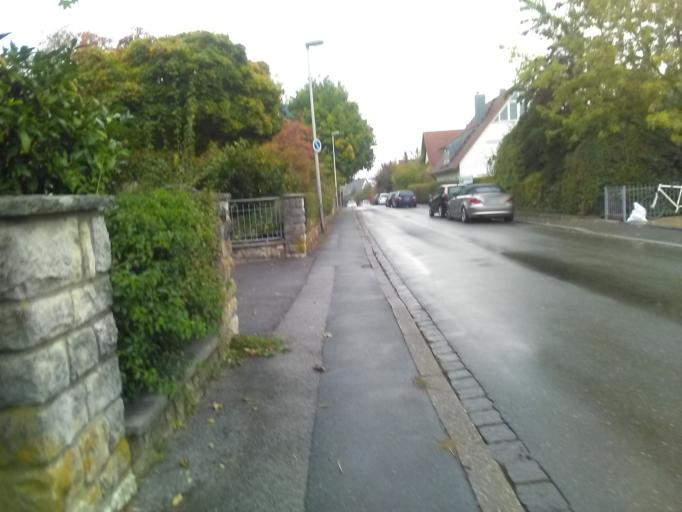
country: DE
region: Bavaria
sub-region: Upper Franconia
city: Bamberg
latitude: 49.8789
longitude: 10.8879
